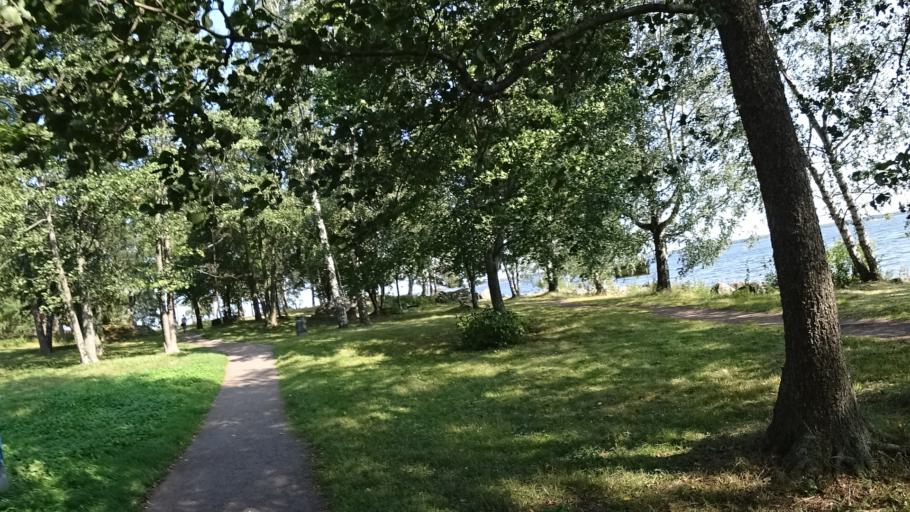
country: FI
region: Kymenlaakso
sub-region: Kotka-Hamina
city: Kotka
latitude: 60.4525
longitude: 26.9491
